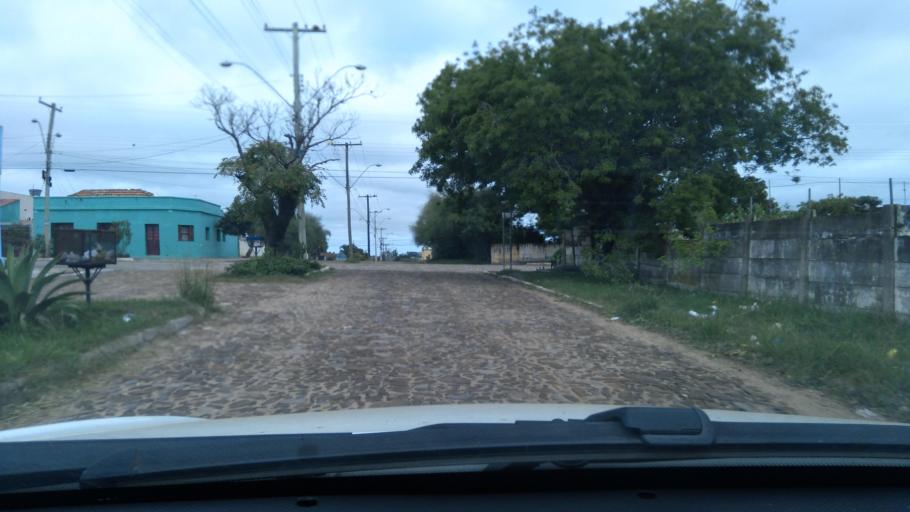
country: BR
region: Rio Grande do Sul
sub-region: Dom Pedrito
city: Dom Pedrito
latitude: -30.9863
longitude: -54.6635
